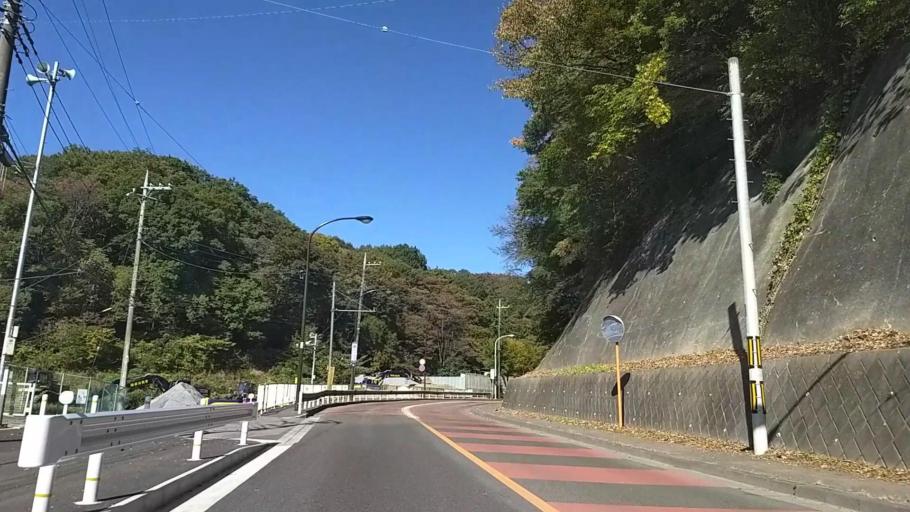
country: JP
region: Tokyo
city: Hachioji
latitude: 35.6194
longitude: 139.2878
